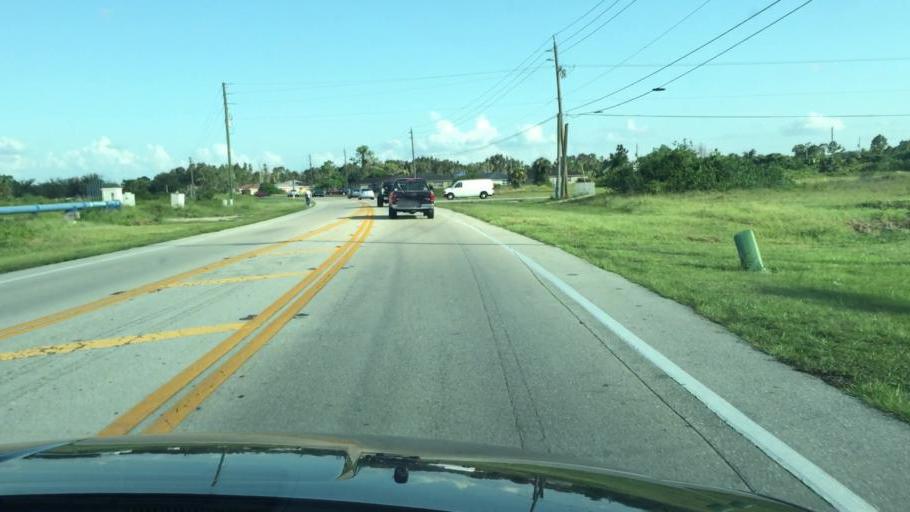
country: US
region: Florida
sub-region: Lee County
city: Gateway
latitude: 26.6136
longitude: -81.7485
